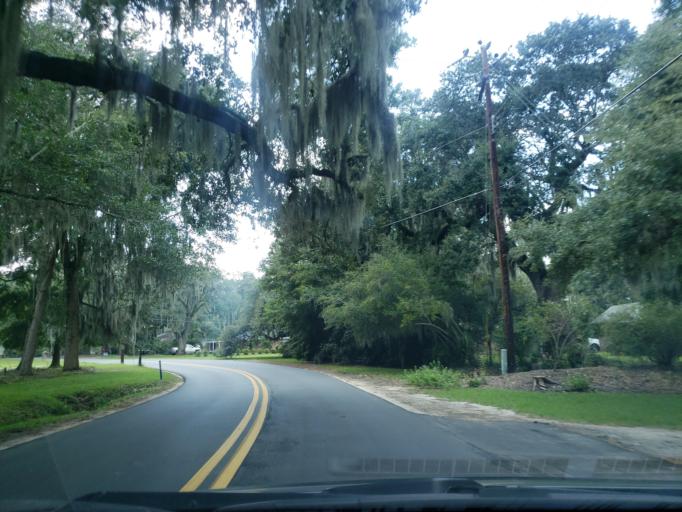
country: US
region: Georgia
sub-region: Chatham County
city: Montgomery
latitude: 31.9316
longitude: -81.0944
